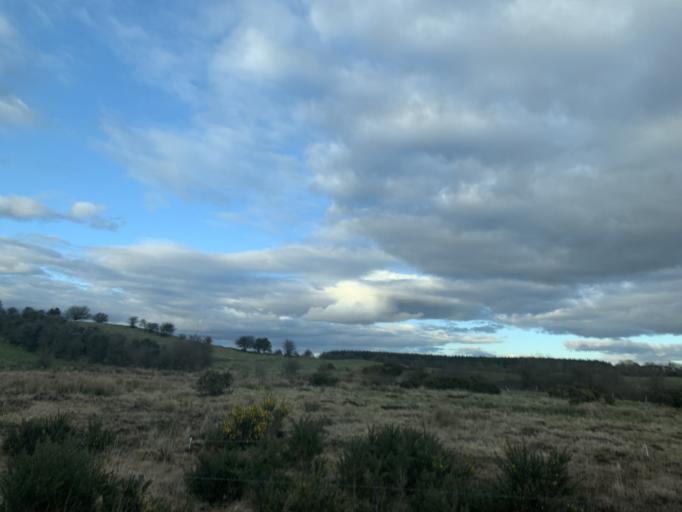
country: IE
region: Connaught
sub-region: Maigh Eo
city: Ballyhaunis
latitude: 53.8393
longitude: -8.7199
